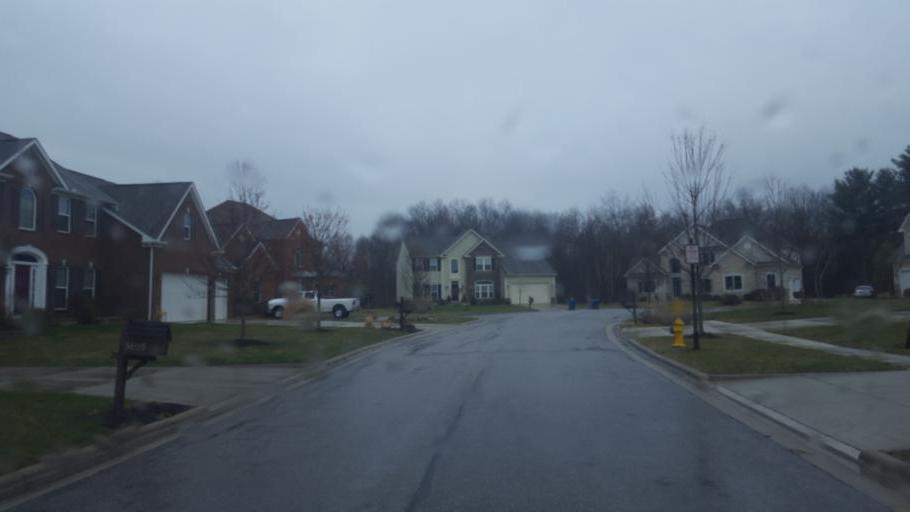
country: US
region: Ohio
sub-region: Delaware County
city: Lewis Center
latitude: 40.2532
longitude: -82.9534
